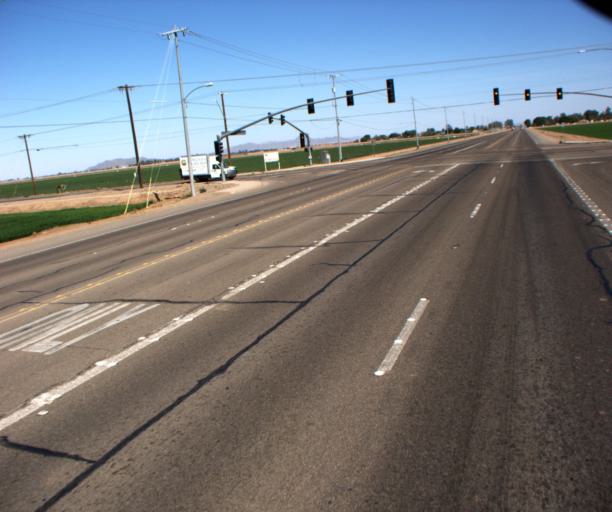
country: US
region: Arizona
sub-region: Yuma County
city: Somerton
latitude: 32.6251
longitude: -114.6498
